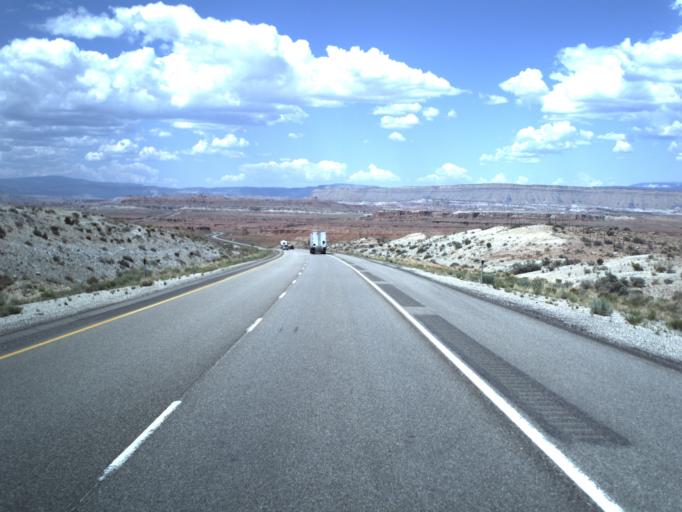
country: US
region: Utah
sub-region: Emery County
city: Ferron
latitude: 38.8479
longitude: -111.0108
